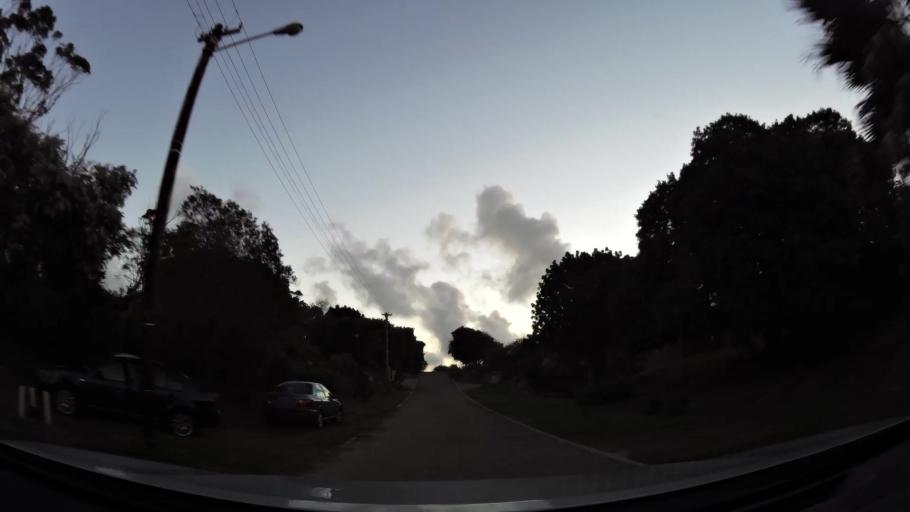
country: ZA
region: Western Cape
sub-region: Eden District Municipality
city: Knysna
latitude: -34.0290
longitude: 22.8089
